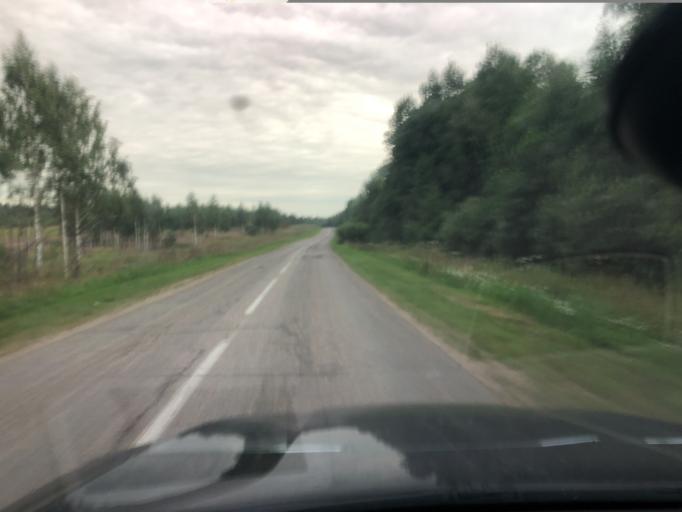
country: RU
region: Jaroslavl
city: Petrovsk
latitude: 57.0013
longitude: 39.0612
